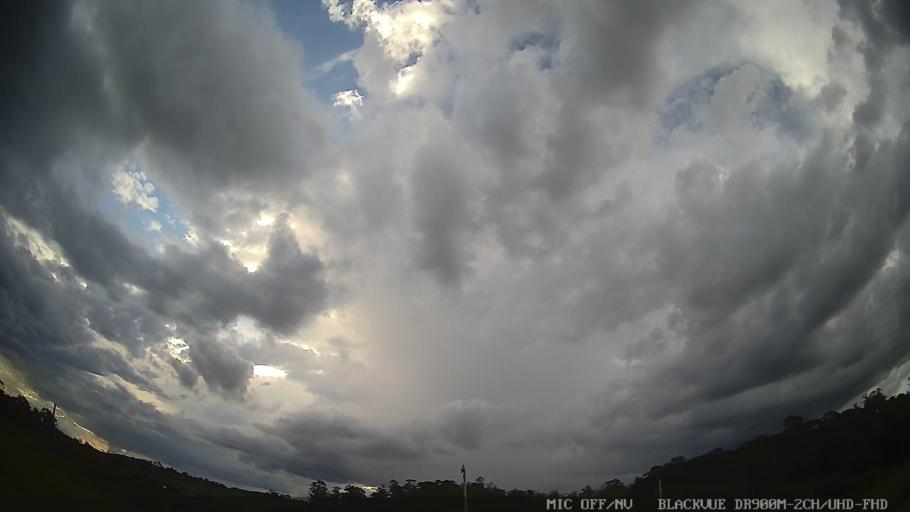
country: BR
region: Sao Paulo
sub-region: Jaguariuna
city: Jaguariuna
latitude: -22.7231
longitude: -47.0143
